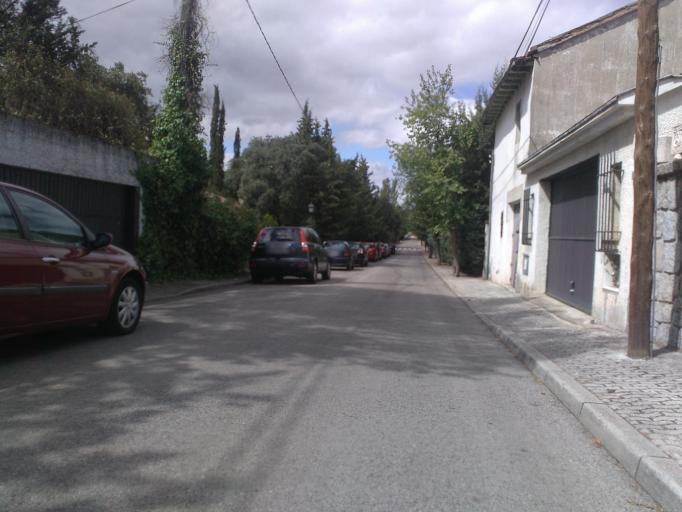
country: ES
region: Madrid
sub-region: Provincia de Madrid
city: Torrelodones
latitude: 40.5810
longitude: -3.9563
